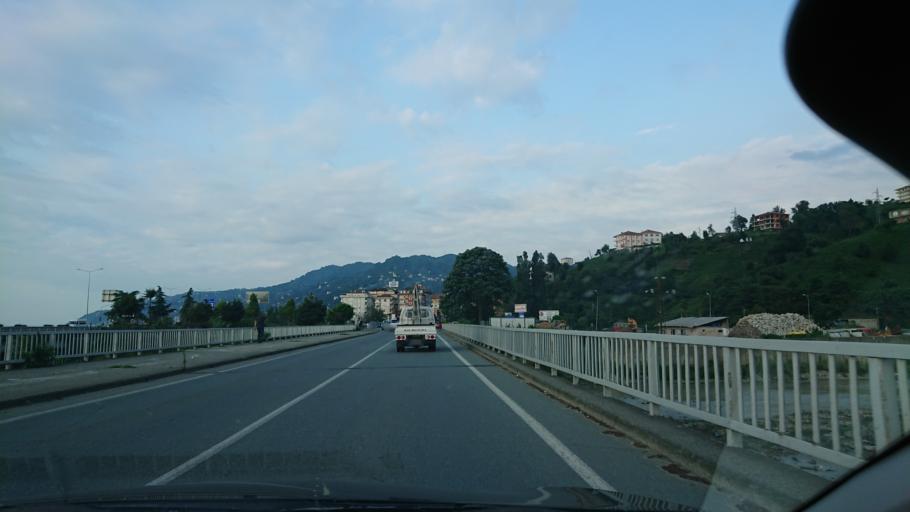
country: TR
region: Rize
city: Cayeli
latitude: 41.0834
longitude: 40.7116
